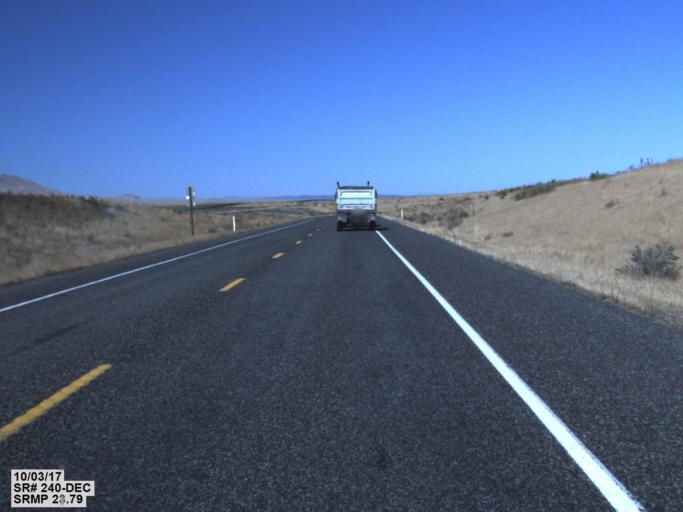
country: US
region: Washington
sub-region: Benton County
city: West Richland
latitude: 46.3536
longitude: -119.3683
